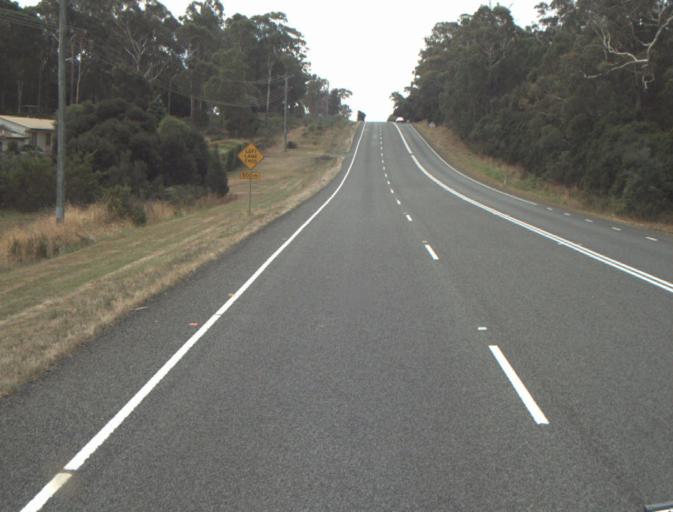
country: AU
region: Tasmania
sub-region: Launceston
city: Mayfield
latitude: -41.2827
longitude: 147.0392
